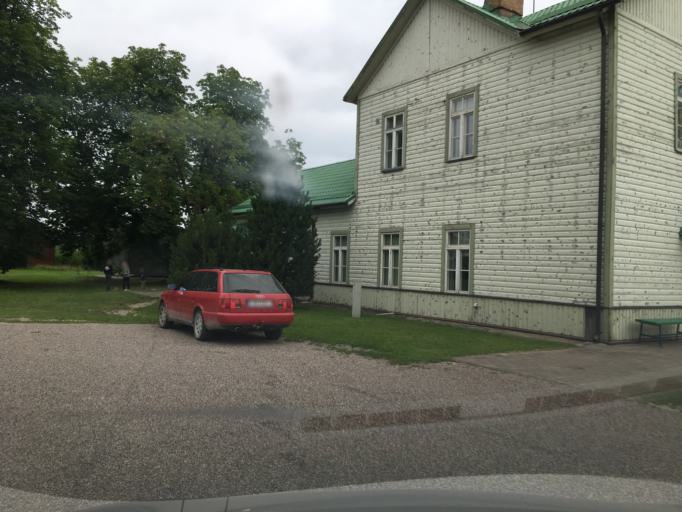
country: EE
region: Raplamaa
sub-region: Kehtna vald
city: Kehtna
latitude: 58.8667
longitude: 25.0081
